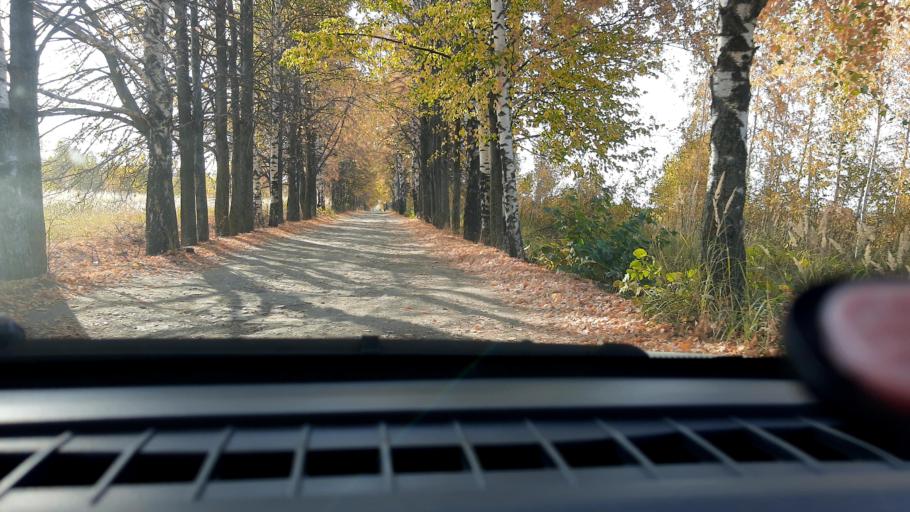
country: RU
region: Nizjnij Novgorod
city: Kstovo
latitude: 56.1504
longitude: 44.2807
